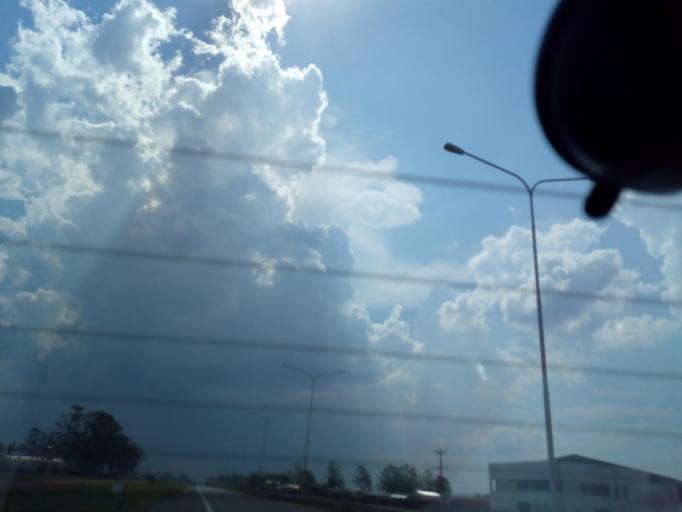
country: AR
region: Corrientes
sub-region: Departamento de Paso de los Libres
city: Paso de los Libres
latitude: -29.7221
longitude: -57.1622
